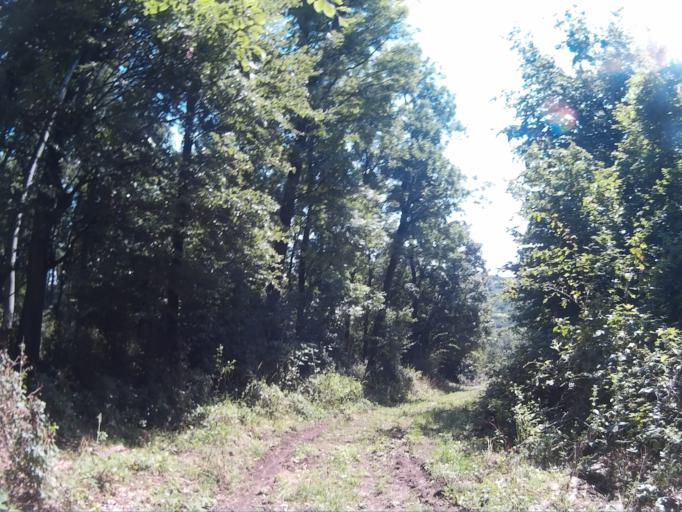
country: HU
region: Veszprem
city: Zirc
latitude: 47.1778
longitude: 17.8700
